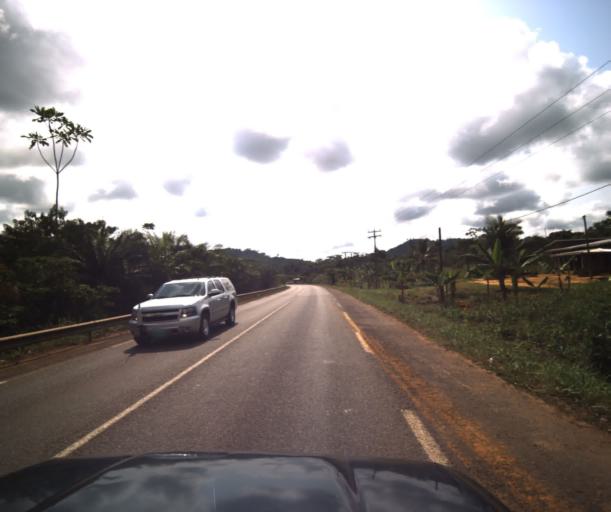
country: CM
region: Littoral
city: Edea
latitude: 3.7652
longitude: 10.1721
